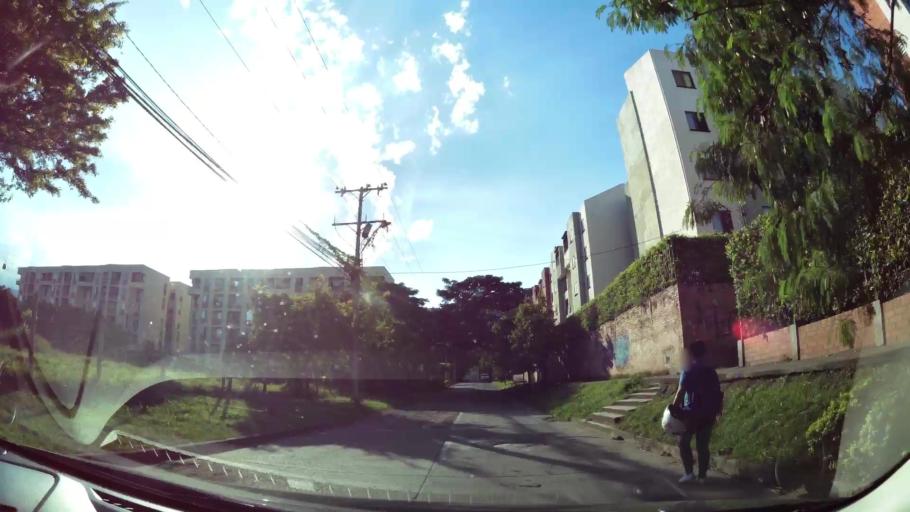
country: CO
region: Valle del Cauca
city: Cali
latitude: 3.4190
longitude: -76.5522
